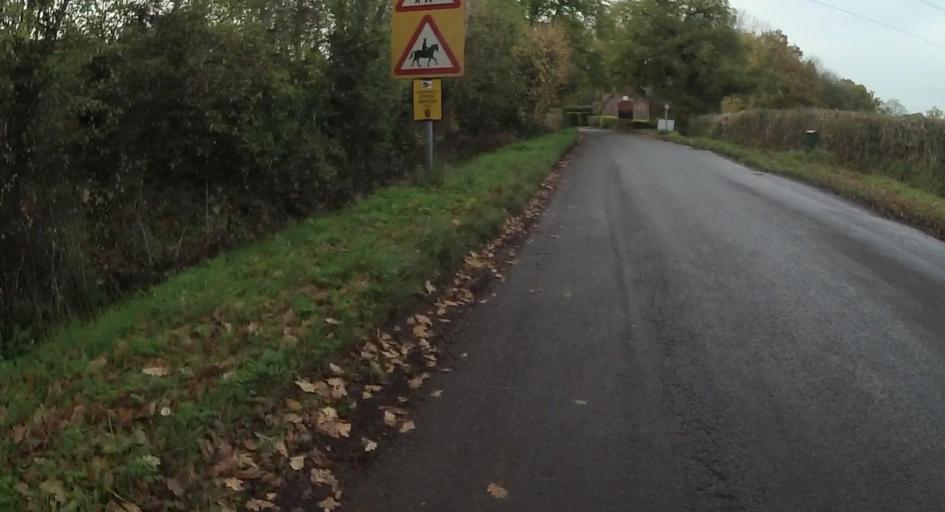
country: GB
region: England
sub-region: West Berkshire
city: Arborfield
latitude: 51.4038
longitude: -0.9085
